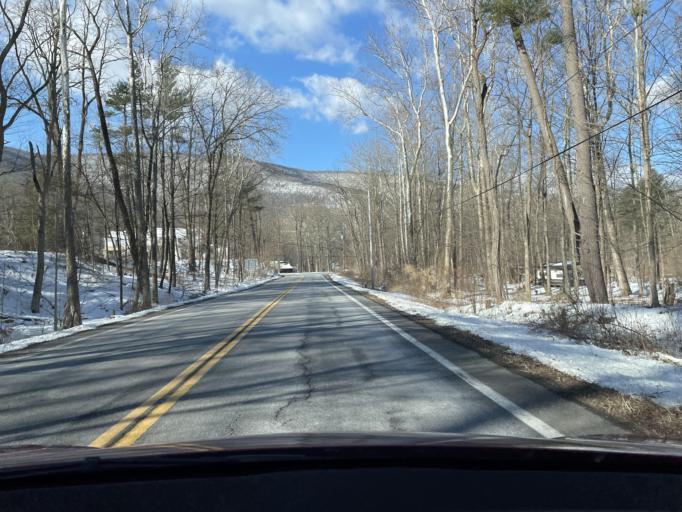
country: US
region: New York
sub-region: Ulster County
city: Shokan
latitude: 42.0466
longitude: -74.2740
